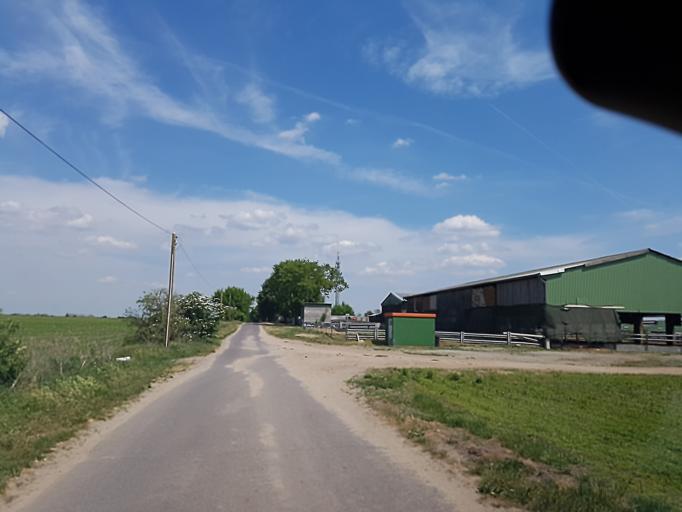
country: DE
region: Brandenburg
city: Gorzke
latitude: 52.1013
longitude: 12.3642
